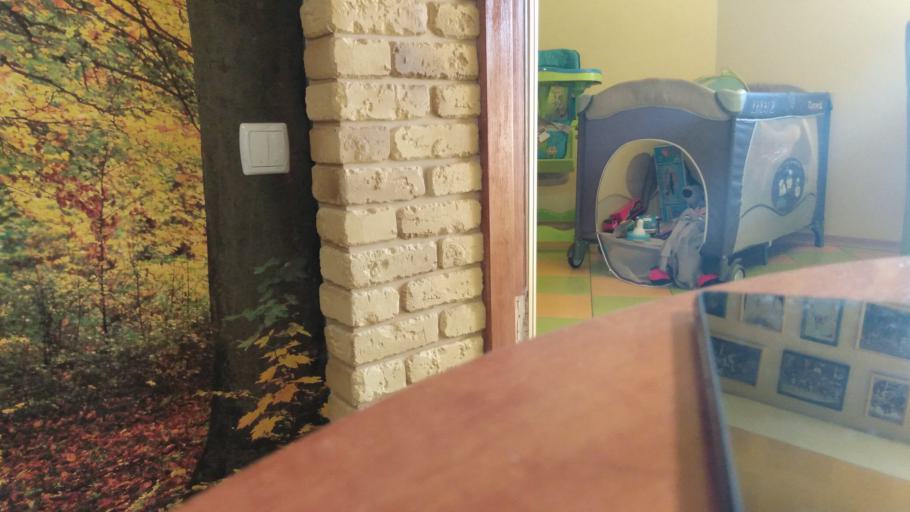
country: RU
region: Tverskaya
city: Bologoye
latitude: 57.9459
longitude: 34.1731
